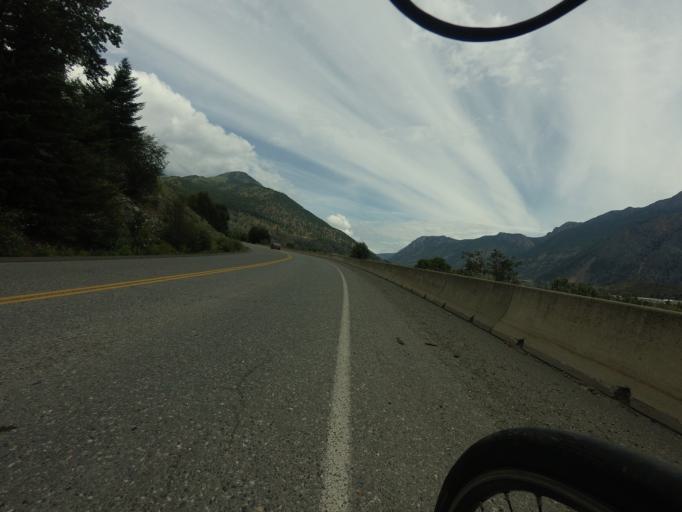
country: CA
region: British Columbia
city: Lillooet
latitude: 50.6822
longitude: -121.9328
